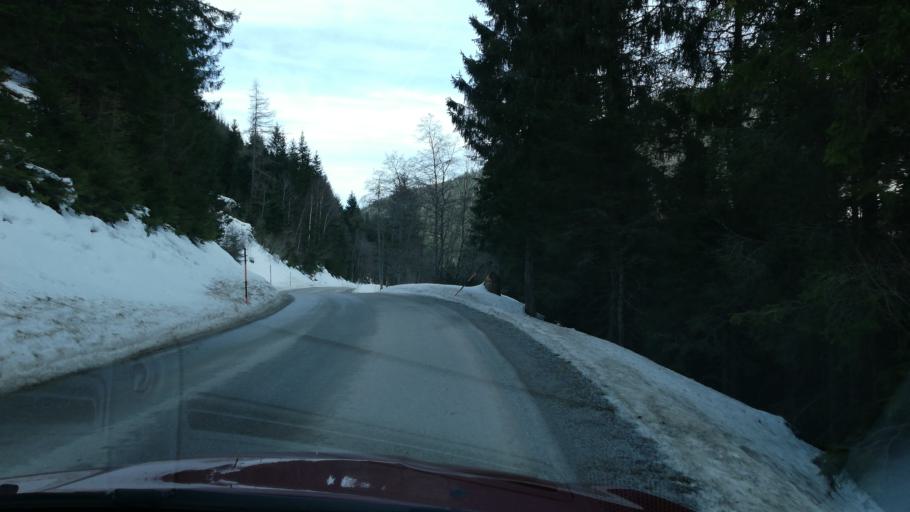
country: AT
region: Styria
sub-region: Politischer Bezirk Liezen
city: Donnersbach
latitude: 47.4278
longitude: 14.1623
